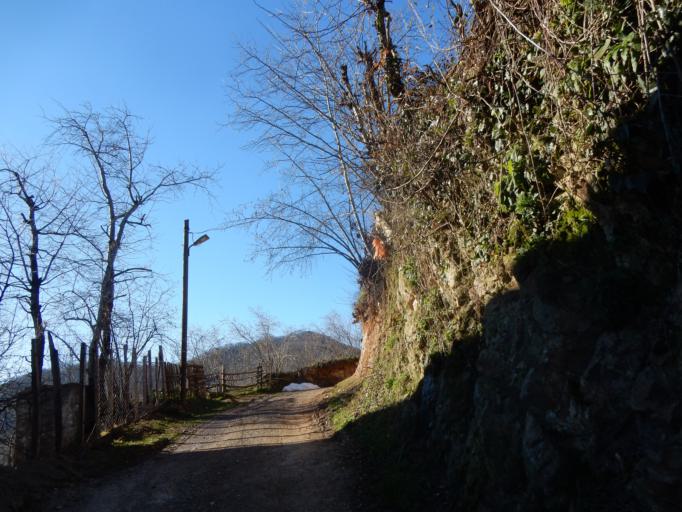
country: TR
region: Ordu
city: Fatsa
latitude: 41.0336
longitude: 37.4147
